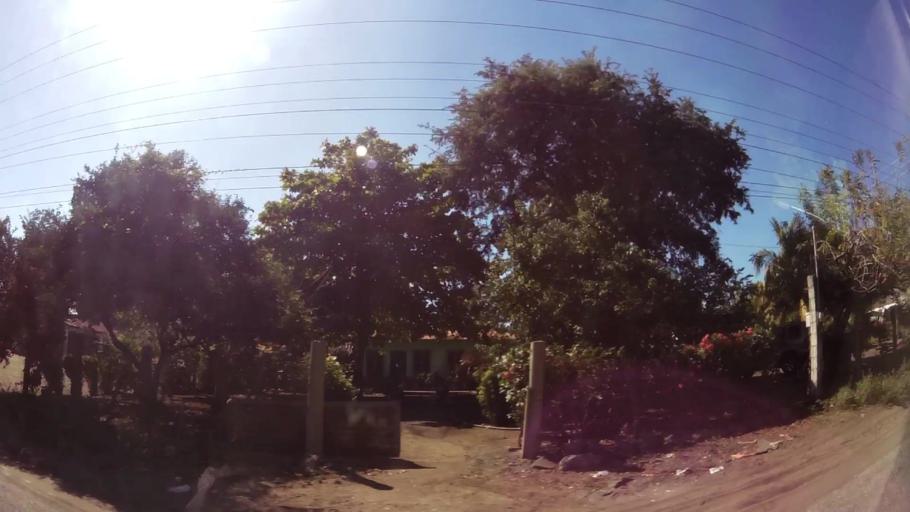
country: GT
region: Escuintla
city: Iztapa
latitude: 13.9207
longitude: -90.5649
